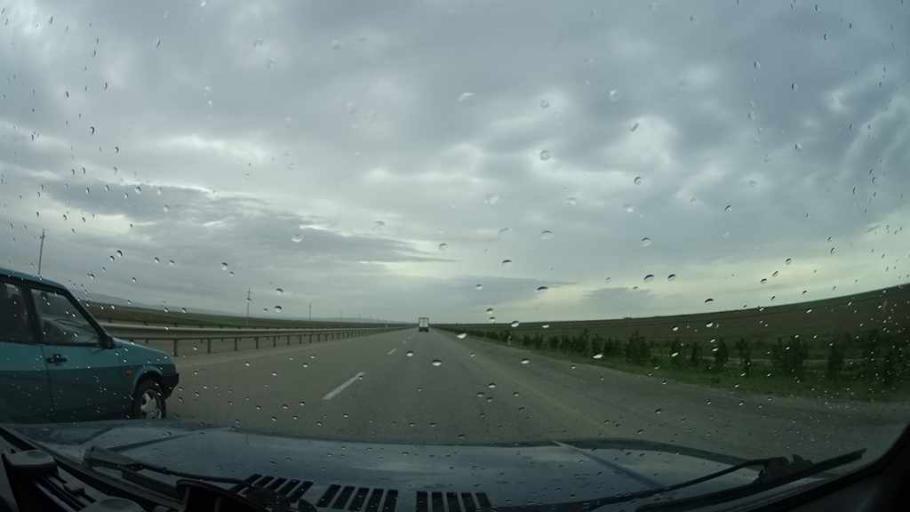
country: AZ
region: Goranboy
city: Goranboy
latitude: 40.6437
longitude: 46.7025
